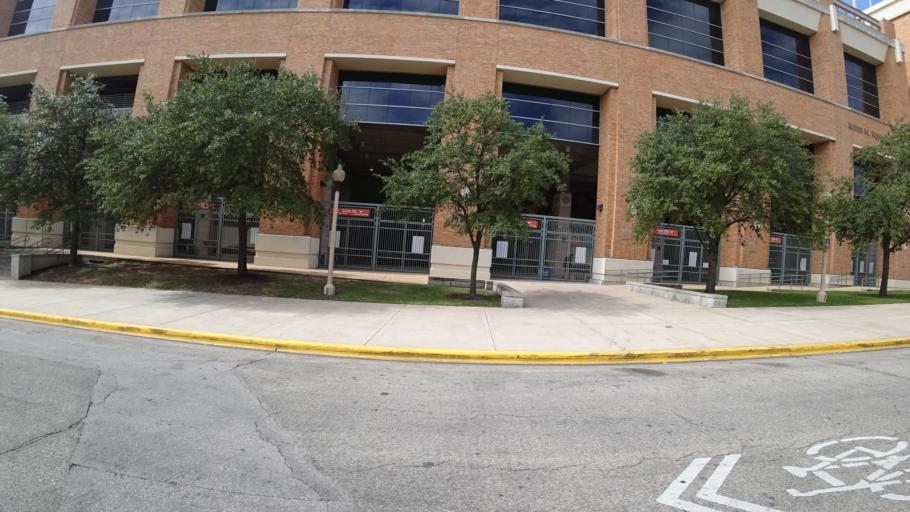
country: US
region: Texas
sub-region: Travis County
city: Austin
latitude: 30.2833
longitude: -97.7312
